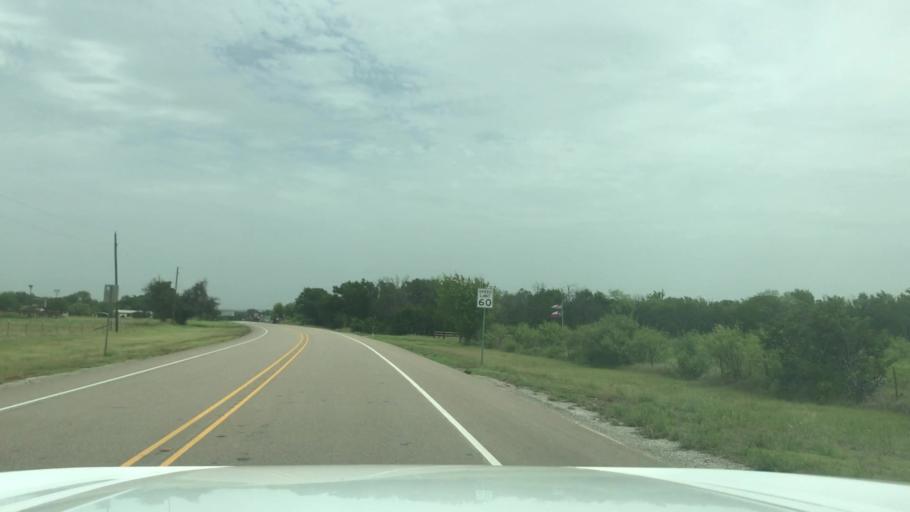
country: US
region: Texas
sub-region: Hamilton County
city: Hico
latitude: 31.9780
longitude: -97.8773
